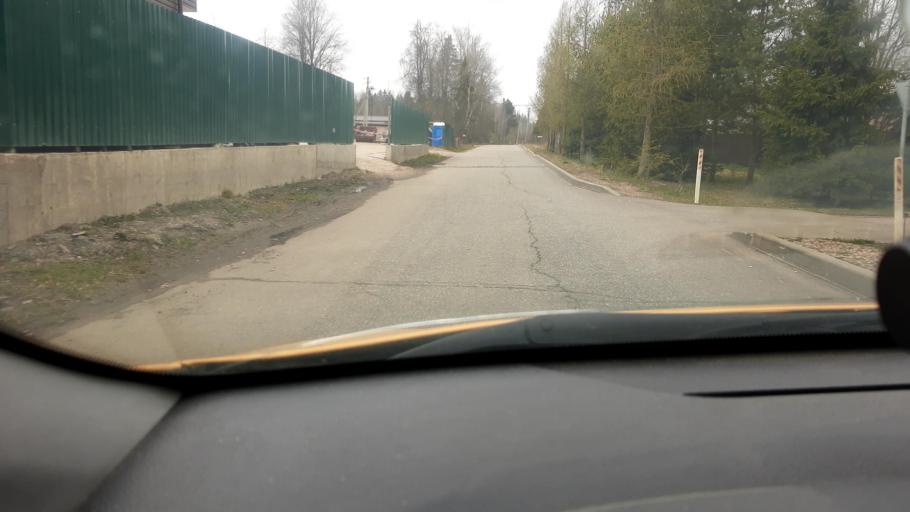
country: RU
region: Moskovskaya
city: Povarovo
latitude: 56.0228
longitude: 36.9915
